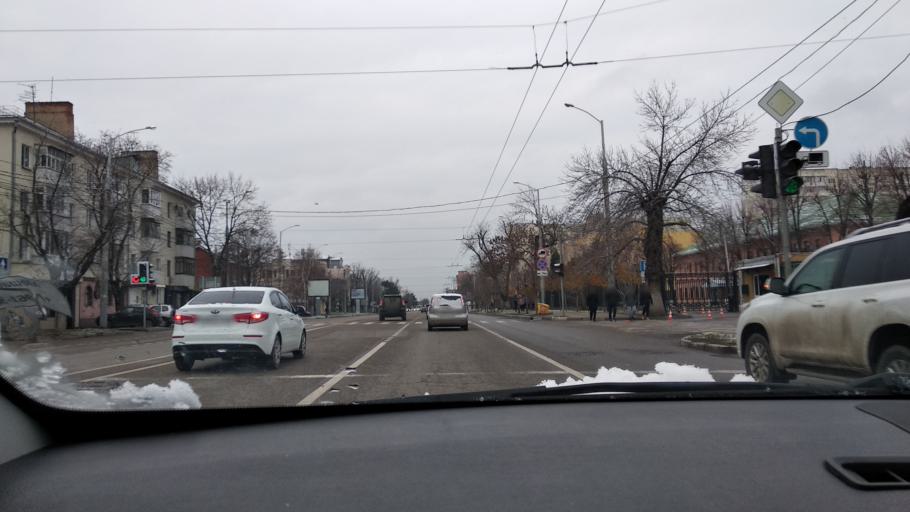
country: RU
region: Krasnodarskiy
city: Krasnodar
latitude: 45.0418
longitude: 38.9656
